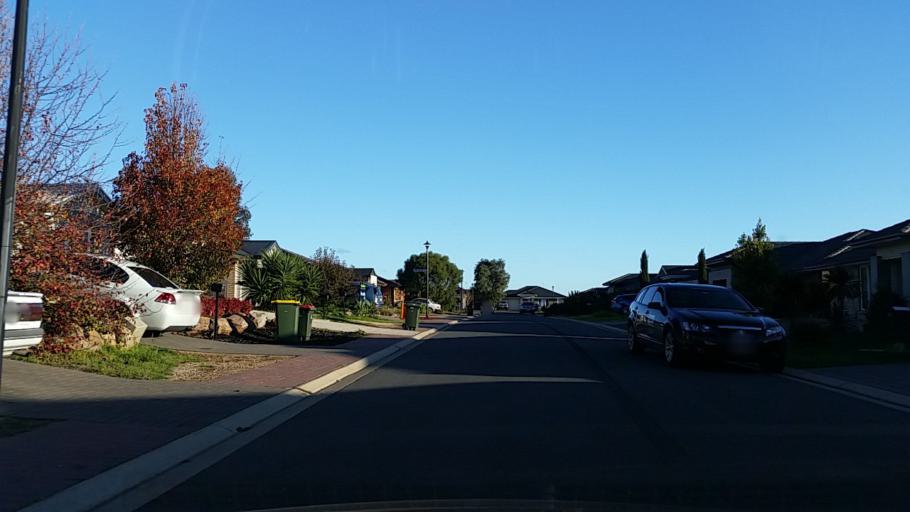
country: AU
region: South Australia
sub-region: Playford
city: Smithfield
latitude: -34.6816
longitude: 138.6842
